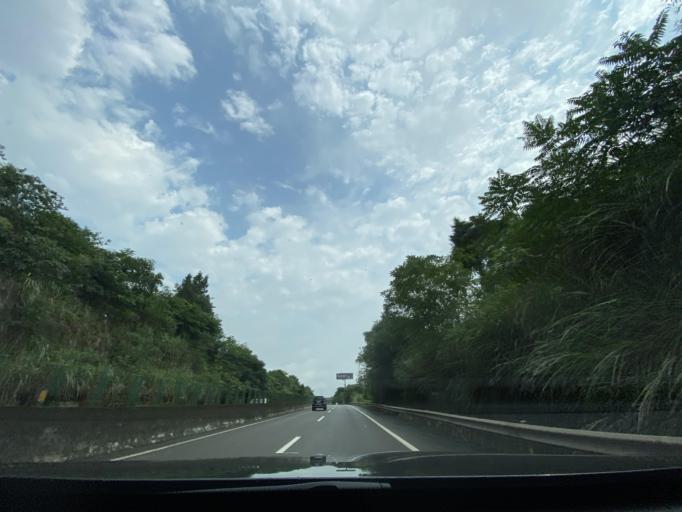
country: CN
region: Sichuan
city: Yanjiang
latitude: 29.9742
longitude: 104.6038
